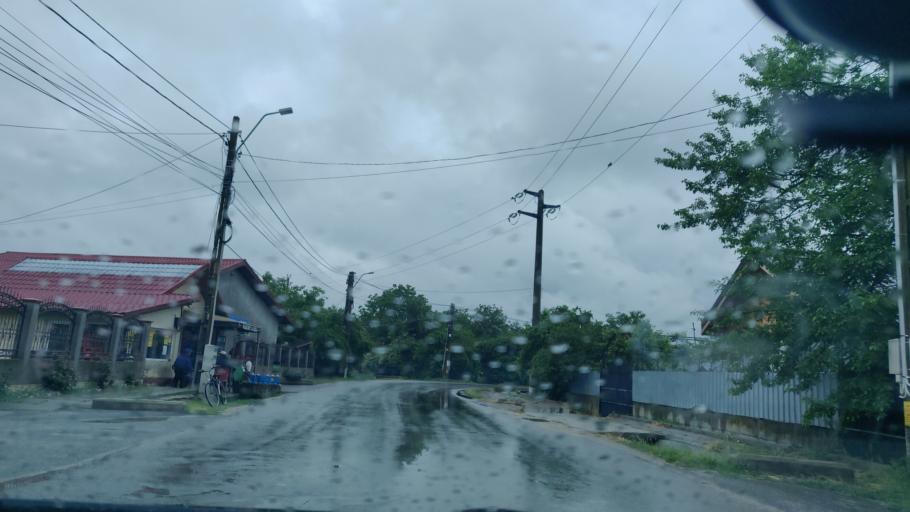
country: RO
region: Giurgiu
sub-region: Comuna Bulbucata
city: Bulbucata
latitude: 44.2857
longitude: 25.8018
